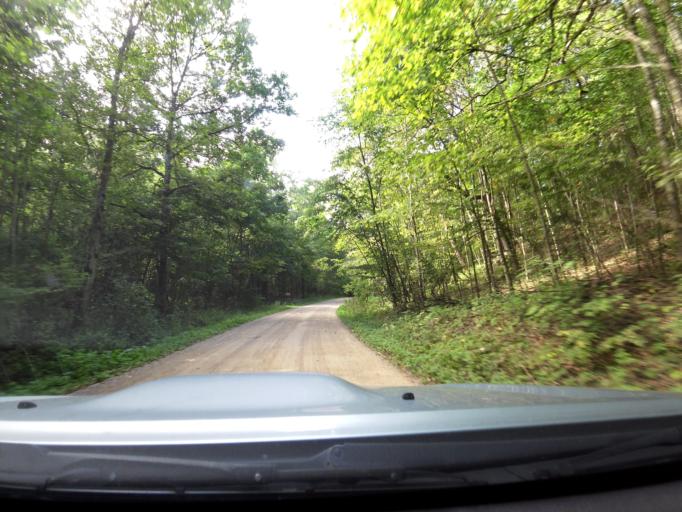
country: LT
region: Vilnius County
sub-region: Vilniaus Rajonas
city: Vievis
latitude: 54.8176
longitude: 24.9675
